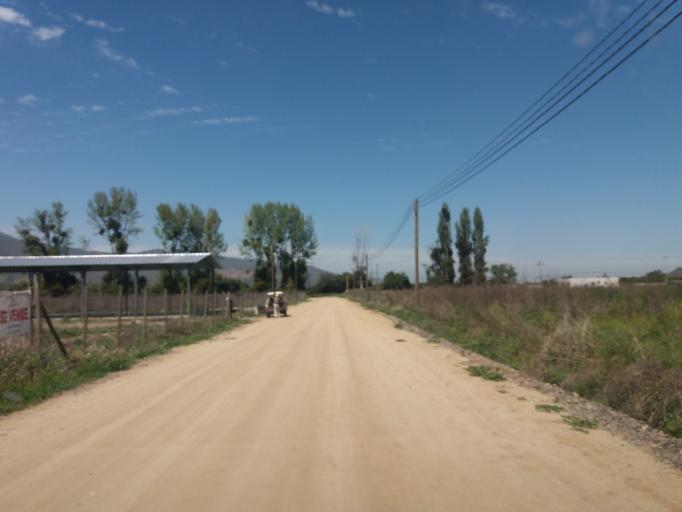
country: CL
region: Valparaiso
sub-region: Provincia de Quillota
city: Quillota
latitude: -32.8768
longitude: -71.2162
